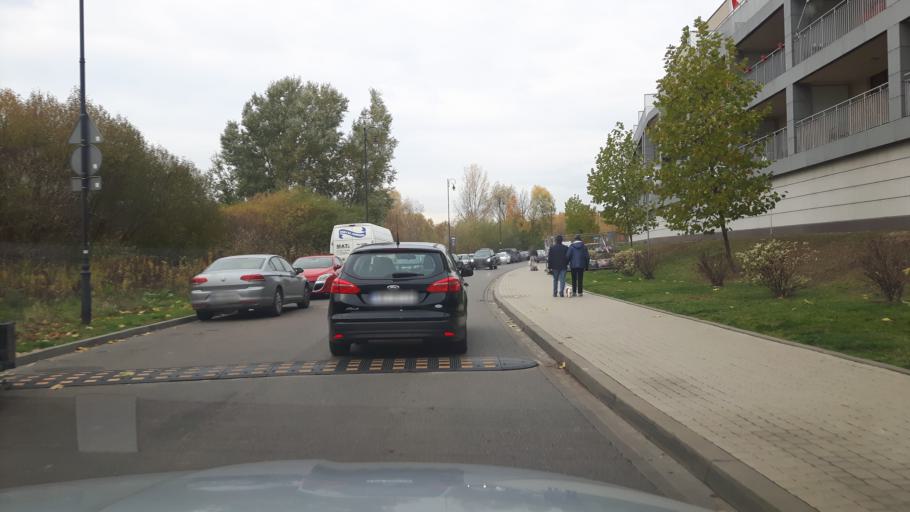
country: PL
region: Masovian Voivodeship
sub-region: Warszawa
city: Ursynow
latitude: 52.1604
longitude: 21.0643
